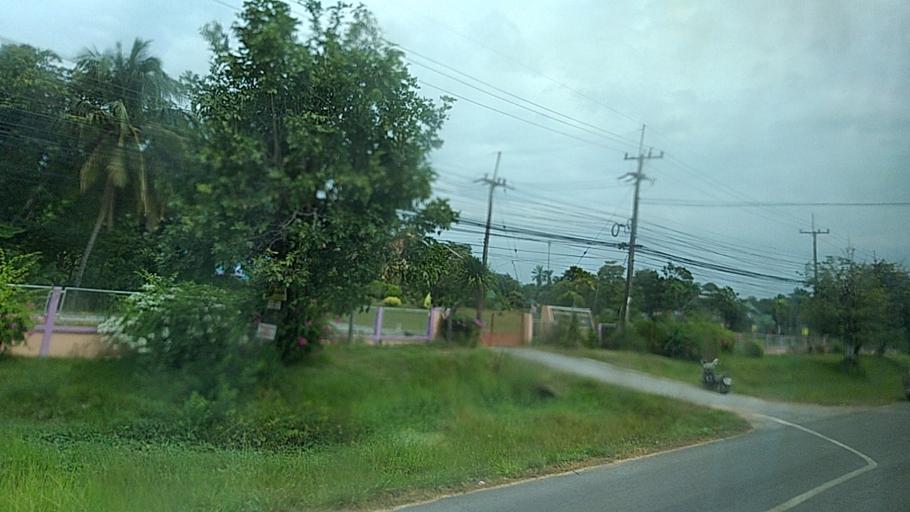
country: TH
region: Roi Et
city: Roi Et
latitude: 16.0707
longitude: 103.6012
